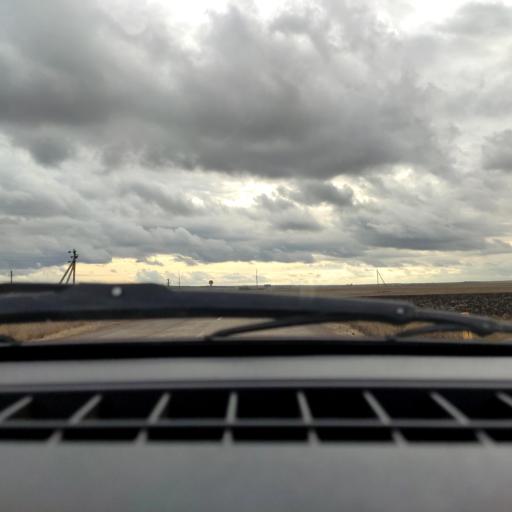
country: RU
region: Bashkortostan
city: Asanovo
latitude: 54.9397
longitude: 55.5172
